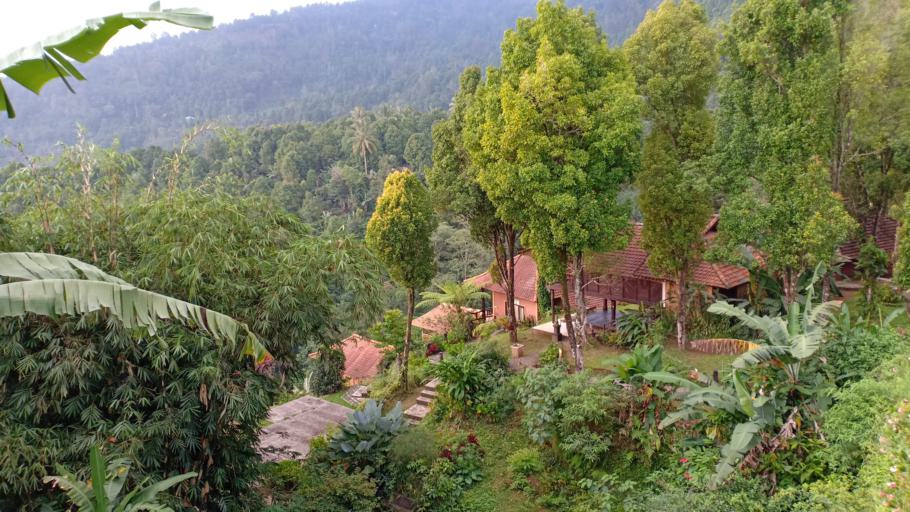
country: ID
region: Bali
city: Munduk
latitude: -8.2613
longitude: 115.0661
